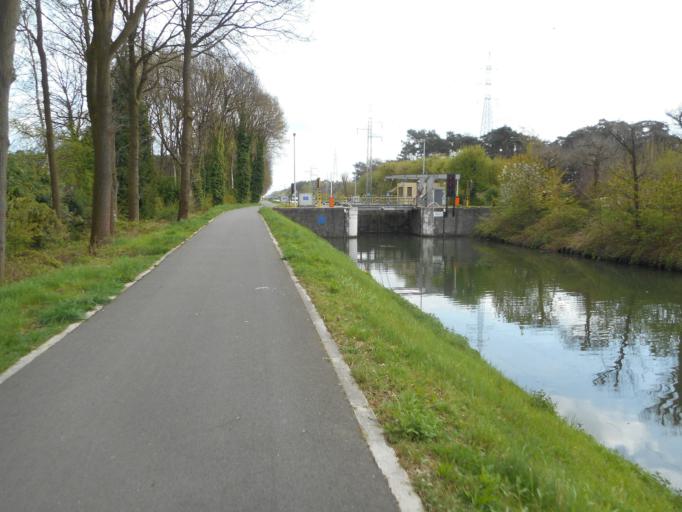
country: BE
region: Flanders
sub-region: Provincie Antwerpen
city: Schilde
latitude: 51.3058
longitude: 4.5780
